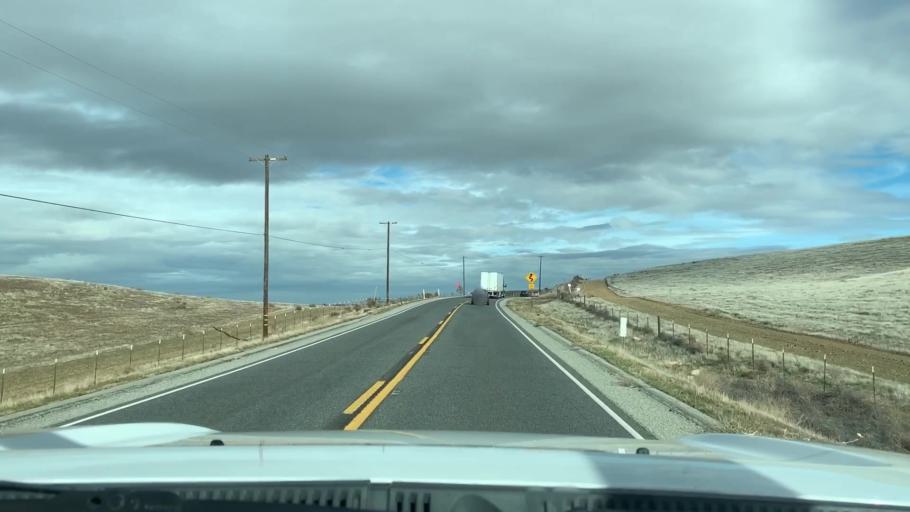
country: US
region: California
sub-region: Kern County
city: Maricopa
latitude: 34.9570
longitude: -119.4496
